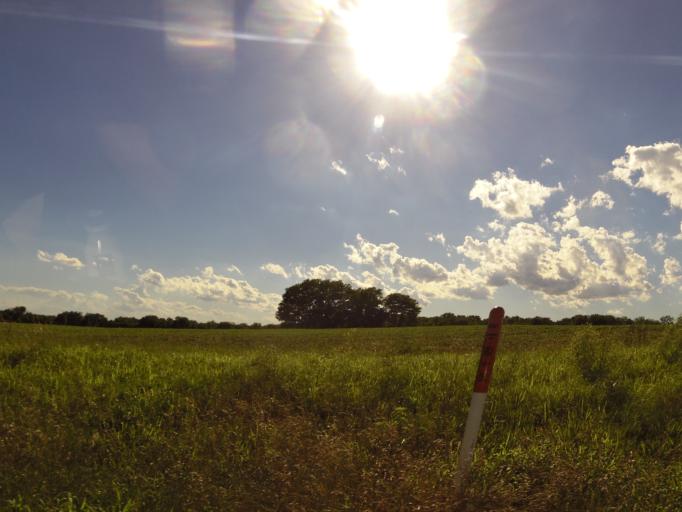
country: US
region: Missouri
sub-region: Marion County
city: Hannibal
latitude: 39.7183
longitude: -91.4485
